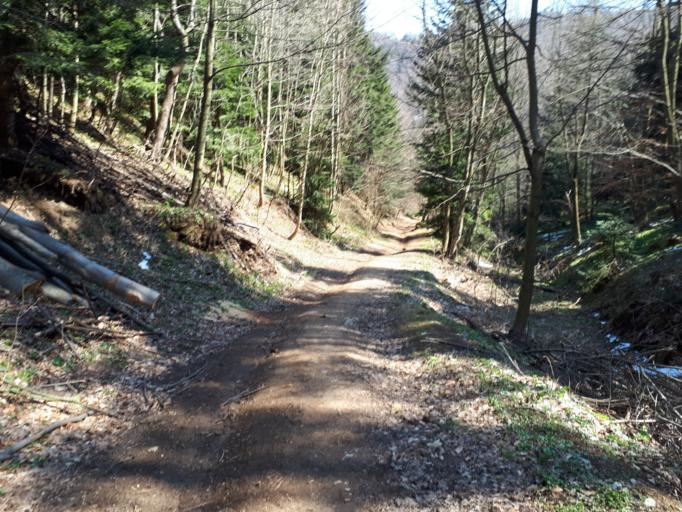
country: HR
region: Varazdinska
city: Ivanec
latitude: 46.1792
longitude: 16.1440
